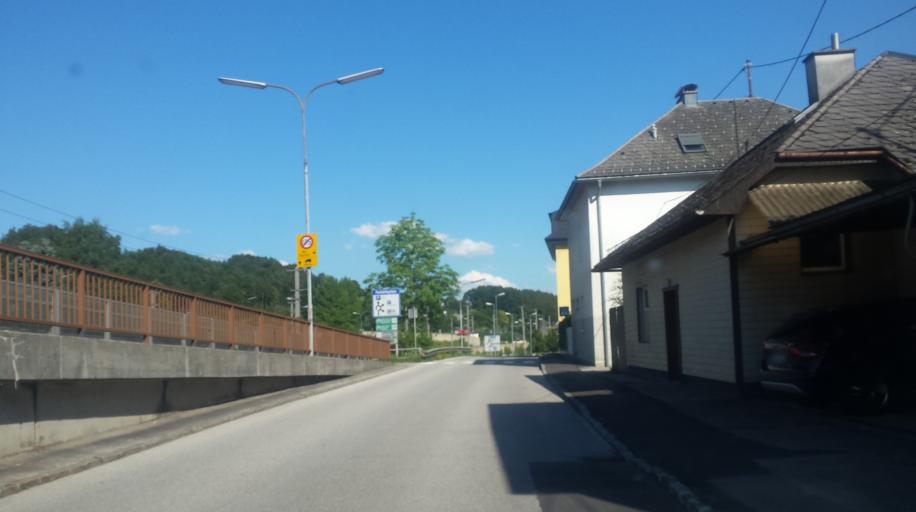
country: AT
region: Upper Austria
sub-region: Politischer Bezirk Vocklabruck
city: Vocklabruck
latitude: 48.0117
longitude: 13.6570
